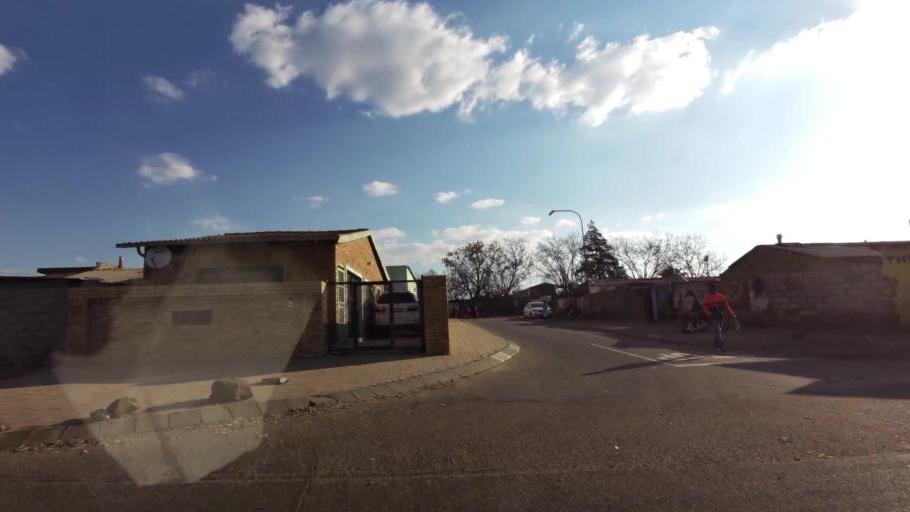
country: ZA
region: Gauteng
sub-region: City of Johannesburg Metropolitan Municipality
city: Soweto
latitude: -26.2322
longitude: 27.9013
